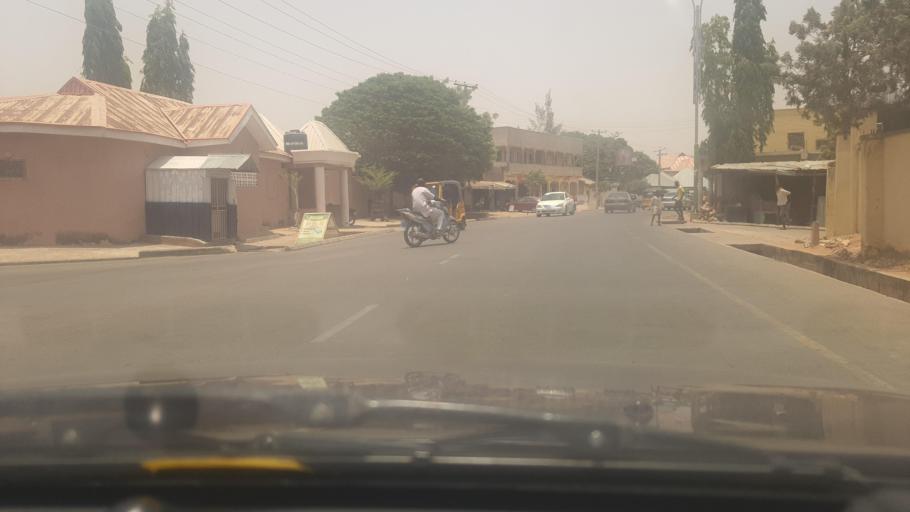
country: NG
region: Gombe
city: Gombe
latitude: 10.2971
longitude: 11.1540
